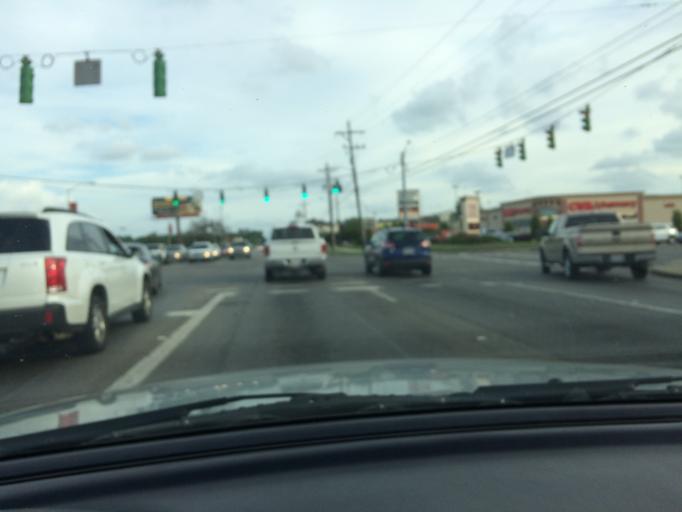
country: US
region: Louisiana
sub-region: Lafayette Parish
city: Lafayette
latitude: 30.2152
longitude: -92.0473
